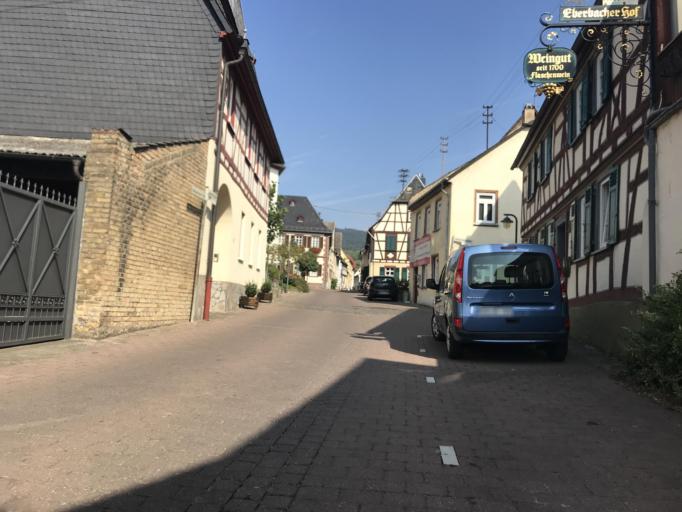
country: DE
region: Rheinland-Pfalz
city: Oestrich-Winkel
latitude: 50.0271
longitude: 8.0315
